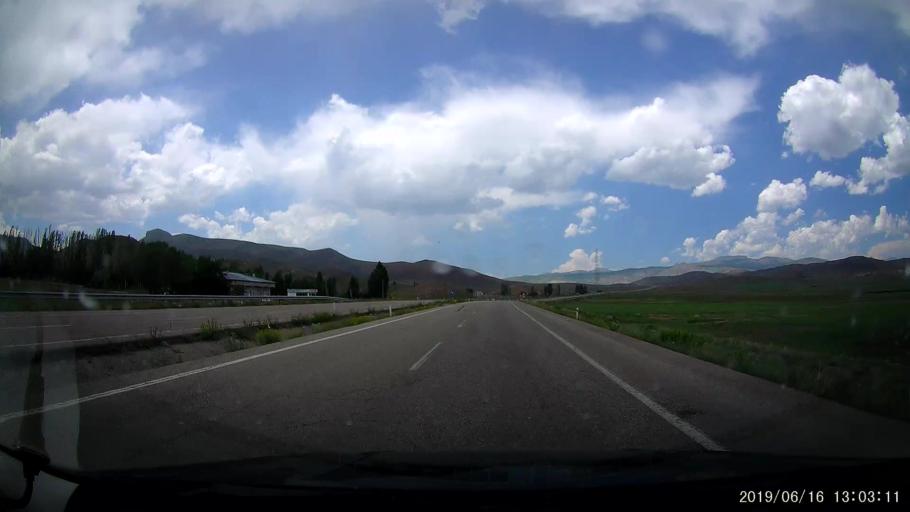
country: TR
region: Agri
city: Sulucem
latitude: 39.5792
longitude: 43.7958
